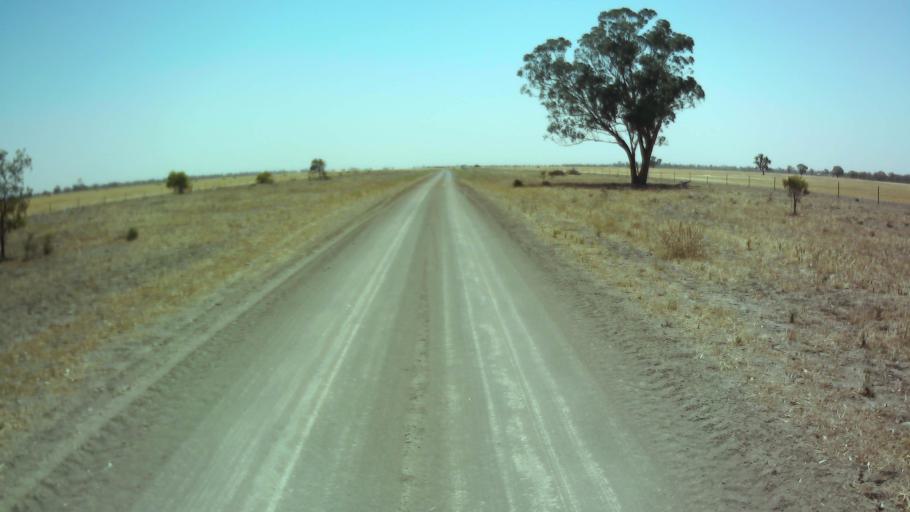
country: AU
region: New South Wales
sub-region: Weddin
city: Grenfell
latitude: -33.9961
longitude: 147.8715
